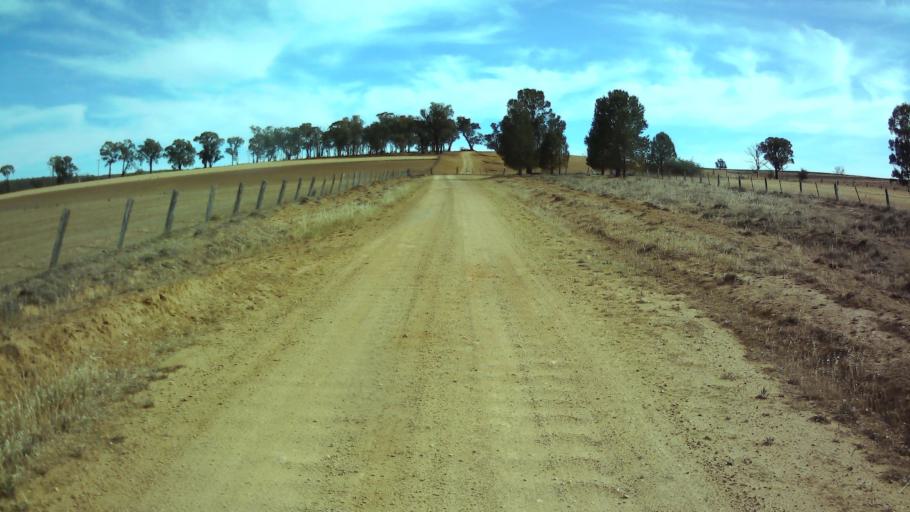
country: AU
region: New South Wales
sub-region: Weddin
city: Grenfell
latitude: -33.8974
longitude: 148.2036
